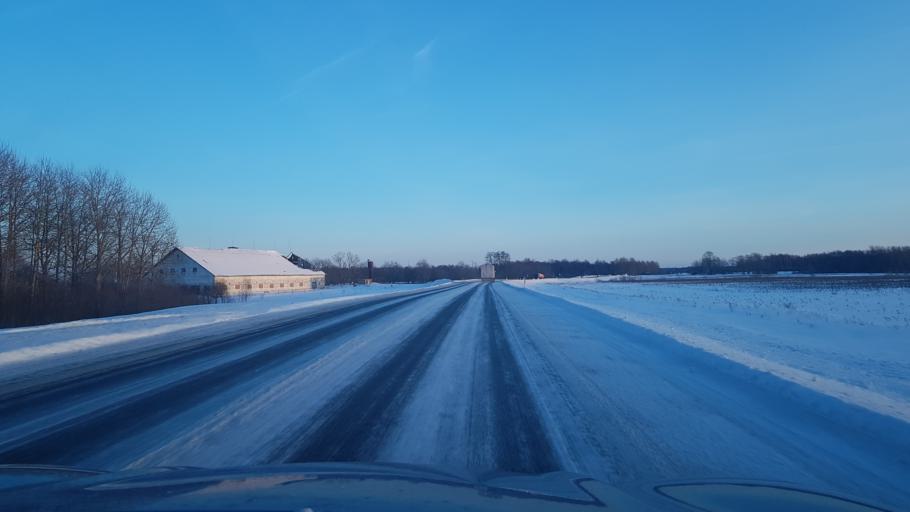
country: EE
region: Ida-Virumaa
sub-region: Narva-Joesuu linn
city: Narva-Joesuu
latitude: 59.4000
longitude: 28.0699
